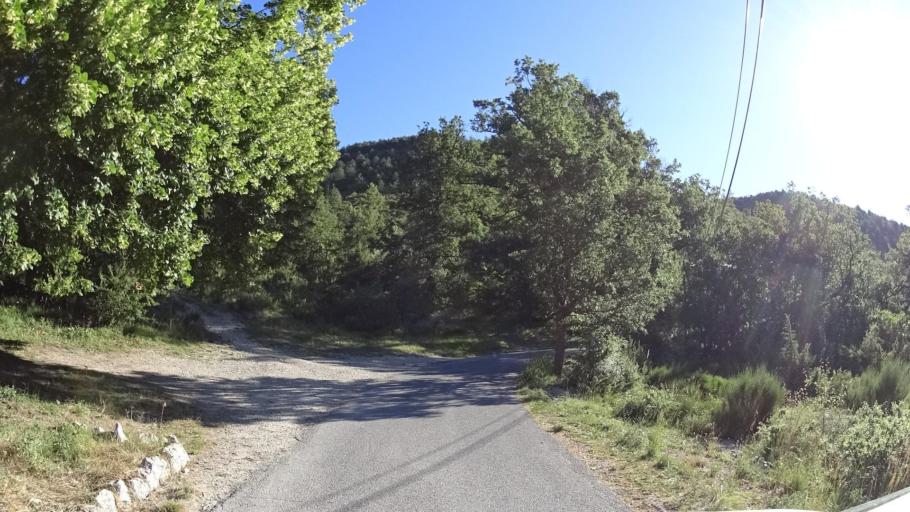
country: FR
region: Provence-Alpes-Cote d'Azur
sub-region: Departement des Alpes-de-Haute-Provence
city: Castellane
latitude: 43.8799
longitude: 6.5025
